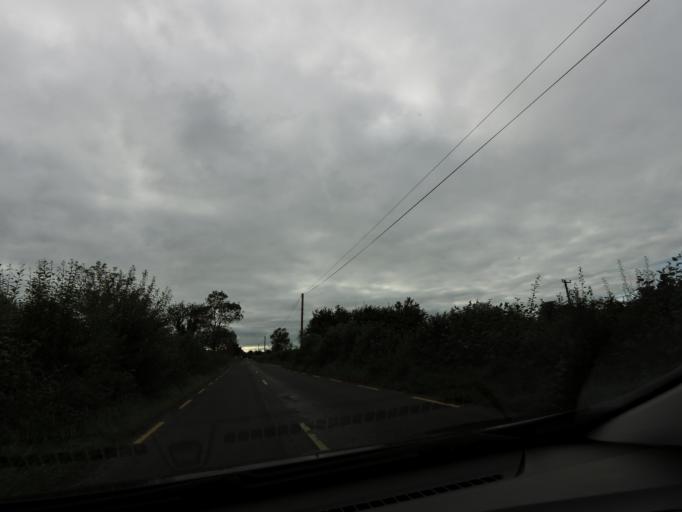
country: IE
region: Leinster
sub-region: Uibh Fhaili
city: Ferbane
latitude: 53.2258
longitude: -7.8120
